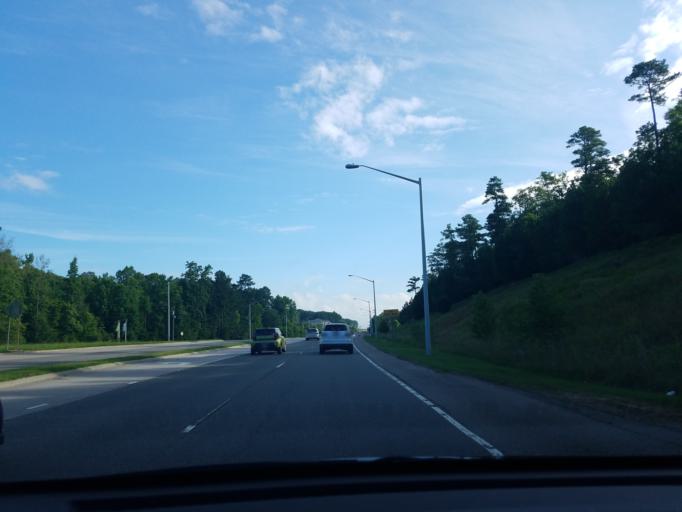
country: US
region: North Carolina
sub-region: Wake County
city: Green Level
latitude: 35.8561
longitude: -78.8946
